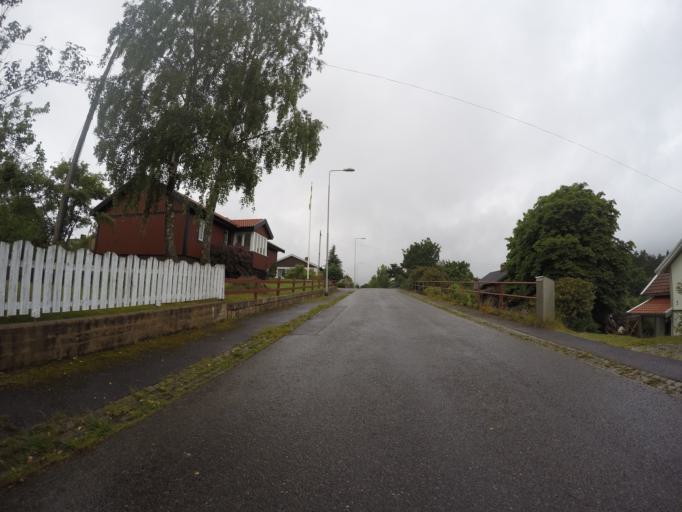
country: SE
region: Vaestra Goetaland
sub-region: Trollhattan
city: Trollhattan
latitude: 58.2645
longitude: 12.2711
